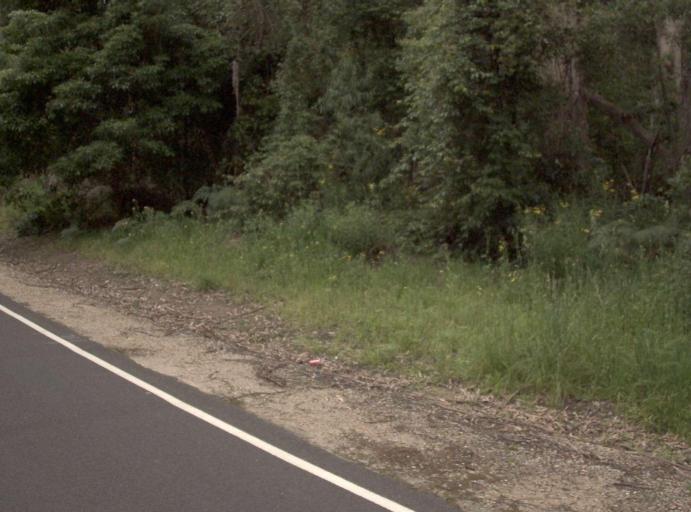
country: AU
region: New South Wales
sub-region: Bombala
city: Bombala
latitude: -37.4622
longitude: 149.1867
